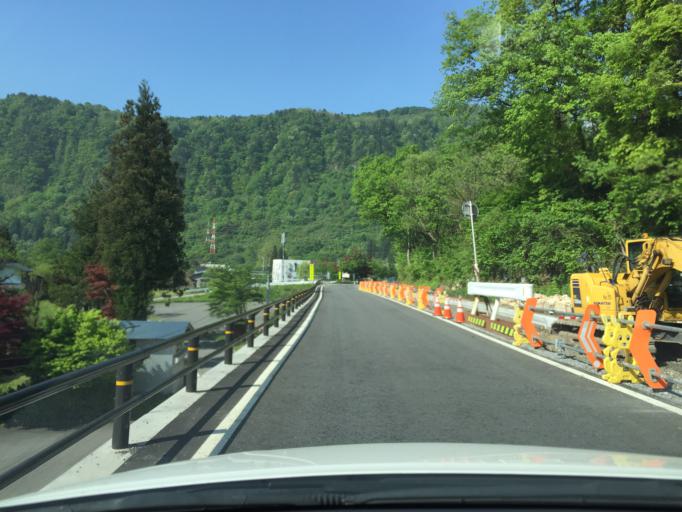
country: JP
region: Niigata
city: Suibara
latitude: 37.7093
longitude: 139.4705
